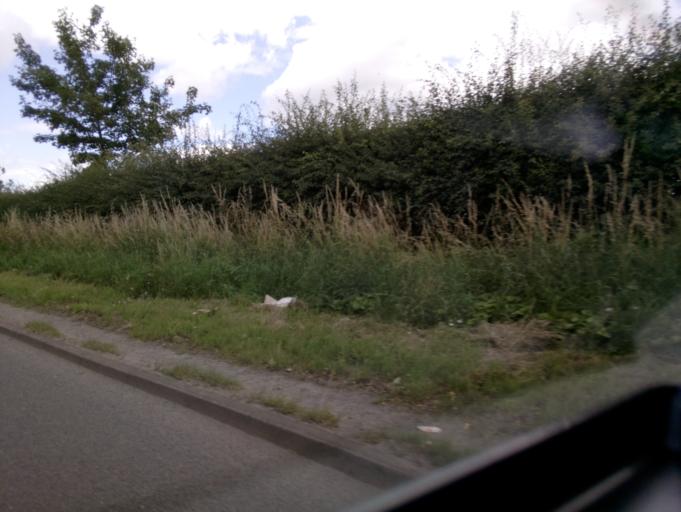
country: GB
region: England
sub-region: Nottinghamshire
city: Ruddington
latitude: 52.8548
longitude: -1.1368
